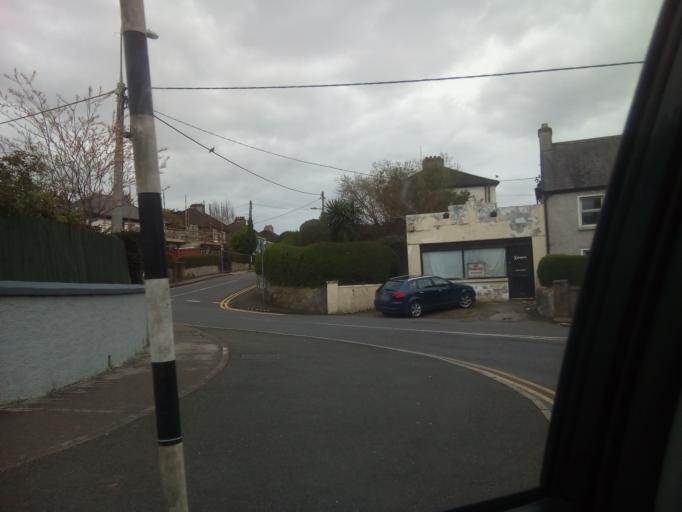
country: IE
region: Munster
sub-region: County Cork
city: Cork
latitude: 51.8890
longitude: -8.5023
